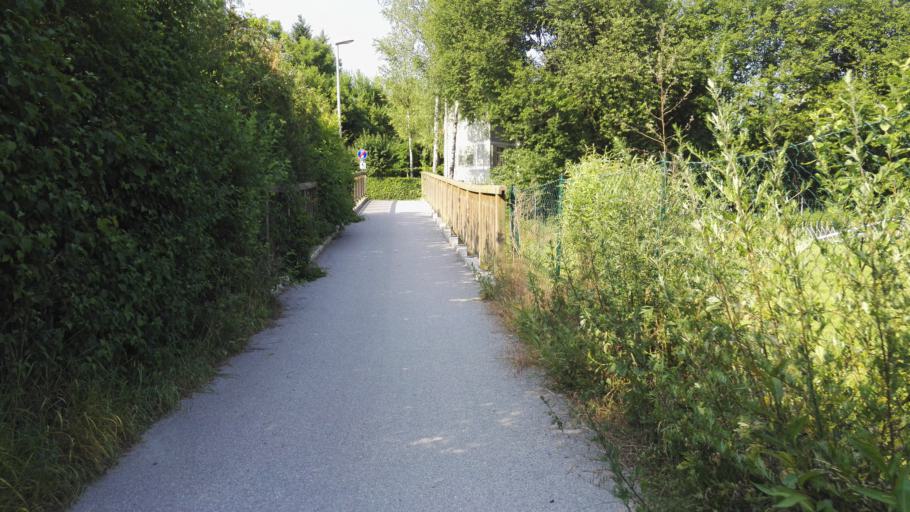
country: AT
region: Styria
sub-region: Graz Stadt
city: Mariatrost
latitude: 47.1088
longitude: 15.4957
